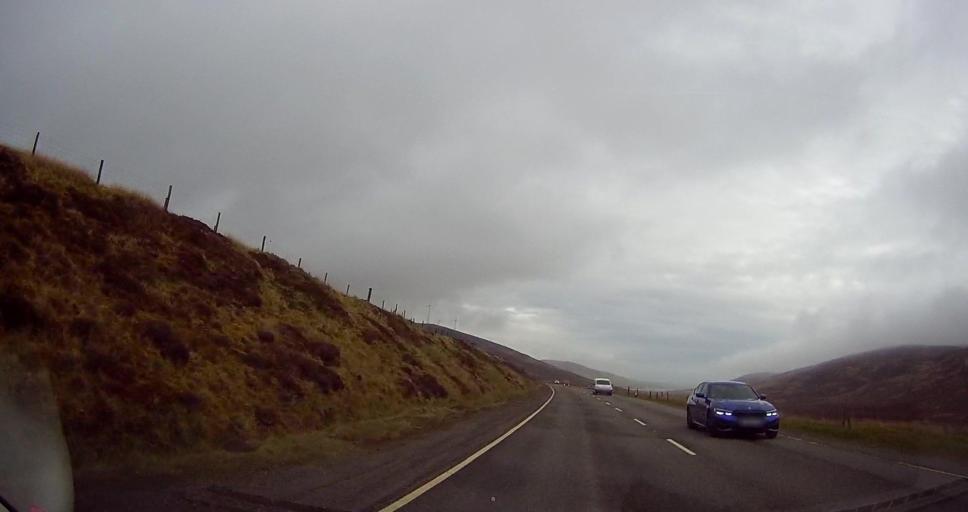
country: GB
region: Scotland
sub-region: Shetland Islands
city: Lerwick
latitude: 60.1482
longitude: -1.2391
